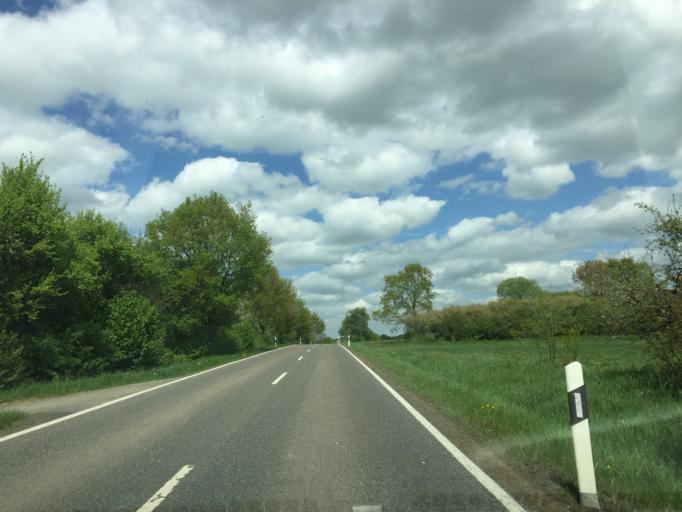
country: DE
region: Rheinland-Pfalz
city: Steinefrenz
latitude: 50.4707
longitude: 7.9343
